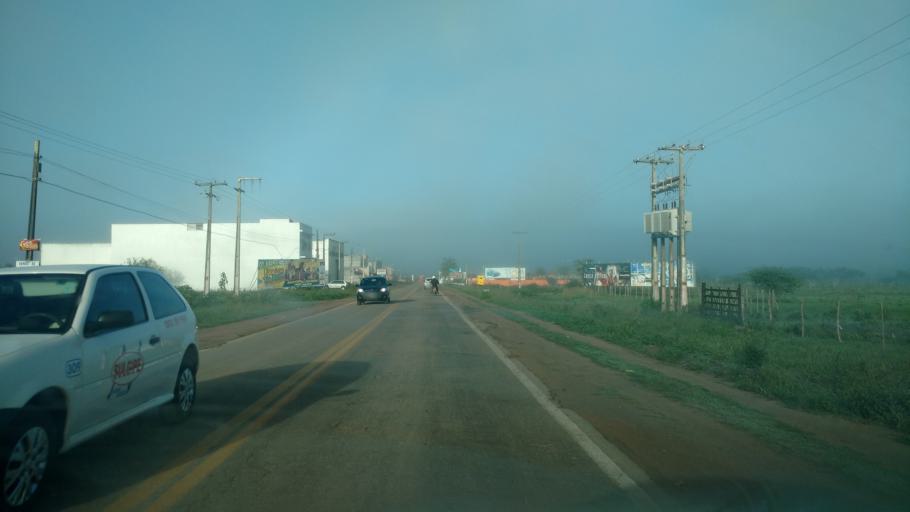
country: BR
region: Sergipe
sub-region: Tobias Barreto
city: Tobias Barreto
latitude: -11.1722
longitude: -37.9873
